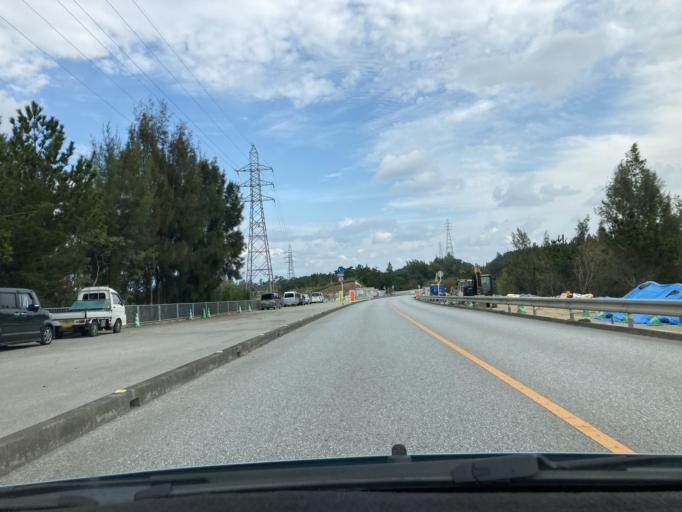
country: JP
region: Okinawa
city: Ishikawa
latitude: 26.4983
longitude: 127.8619
